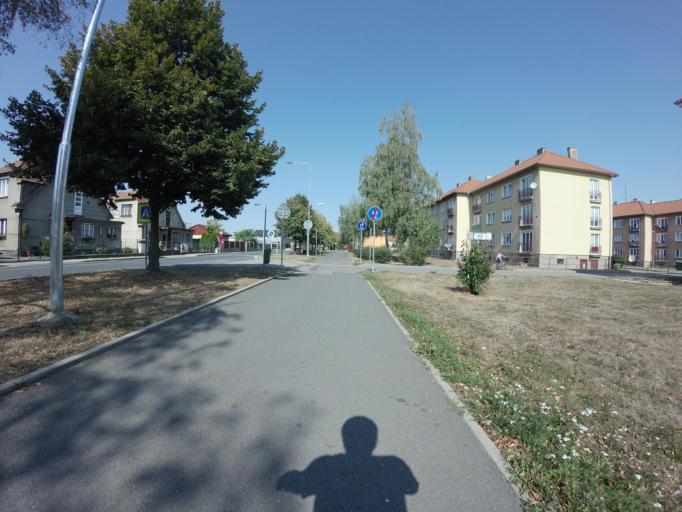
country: CZ
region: Central Bohemia
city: Tynec nad Sazavou
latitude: 49.8364
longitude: 14.5847
